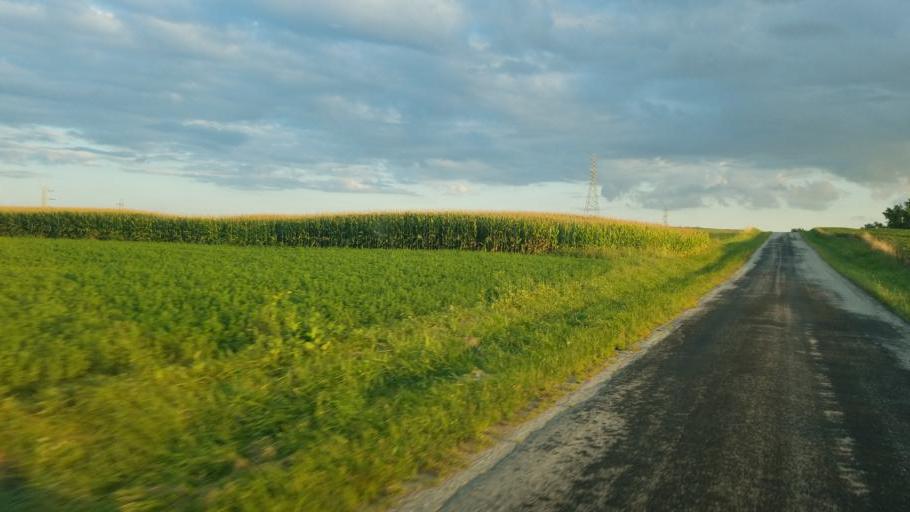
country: US
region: Ohio
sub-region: Richland County
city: Lincoln Heights
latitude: 40.8558
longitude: -82.5328
